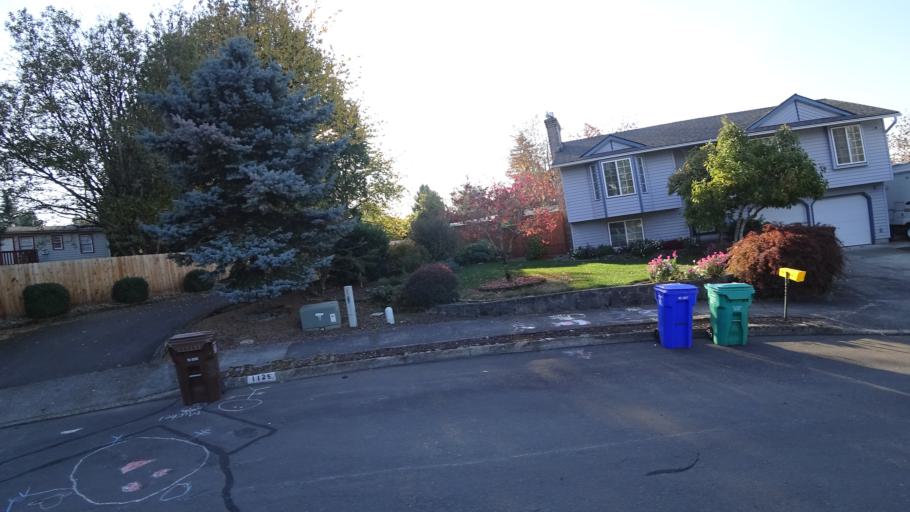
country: US
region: Oregon
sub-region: Multnomah County
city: Gresham
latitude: 45.5051
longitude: -122.4504
